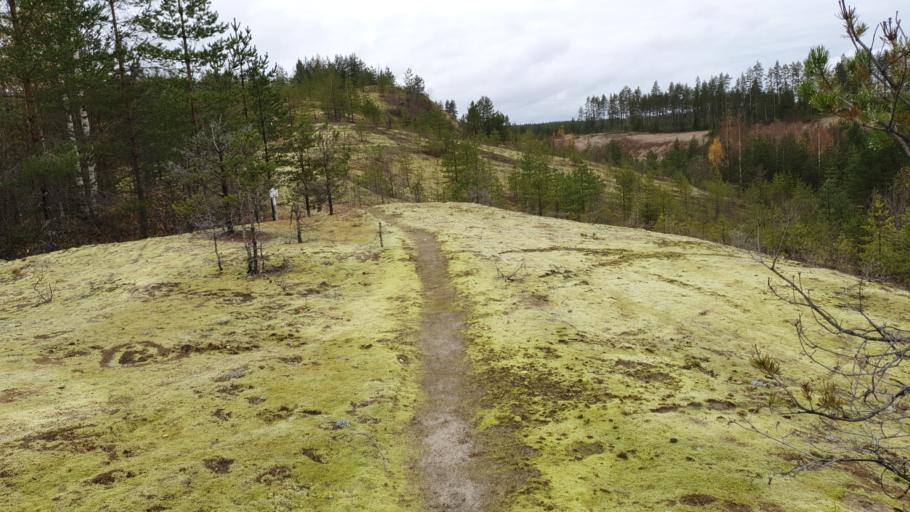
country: FI
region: Kainuu
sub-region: Kehys-Kainuu
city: Kuhmo
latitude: 64.1518
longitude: 29.3955
